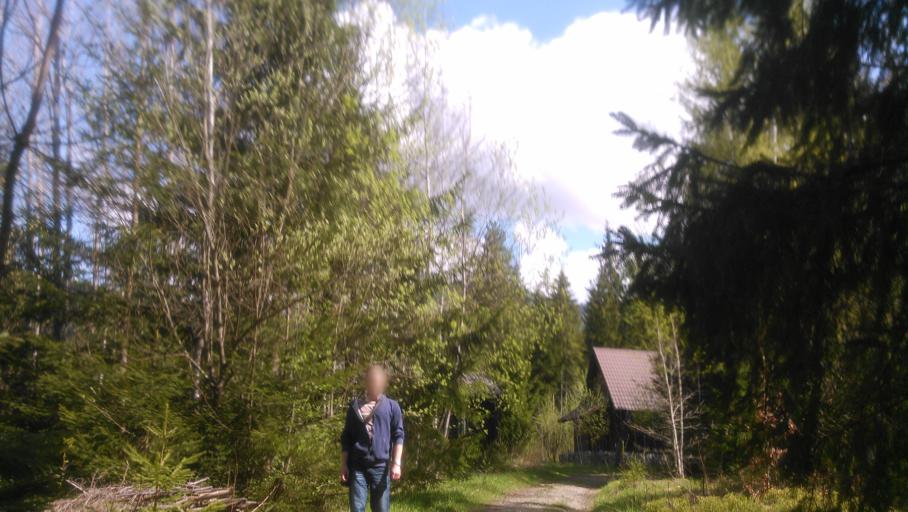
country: SK
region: Banskobystricky
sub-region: Okres Banska Bystrica
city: Brezno
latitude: 48.8689
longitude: 19.5970
